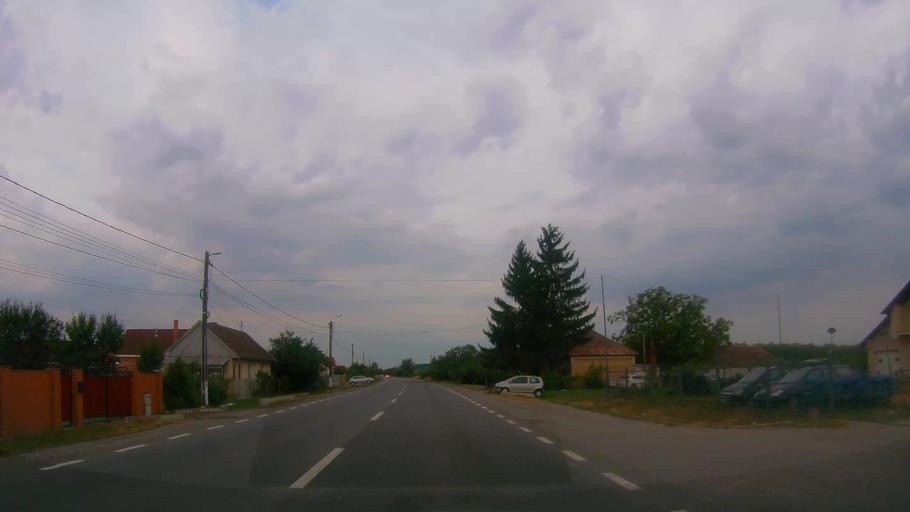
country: RO
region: Satu Mare
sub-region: Comuna Agris
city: Agris
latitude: 47.8712
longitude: 23.0225
